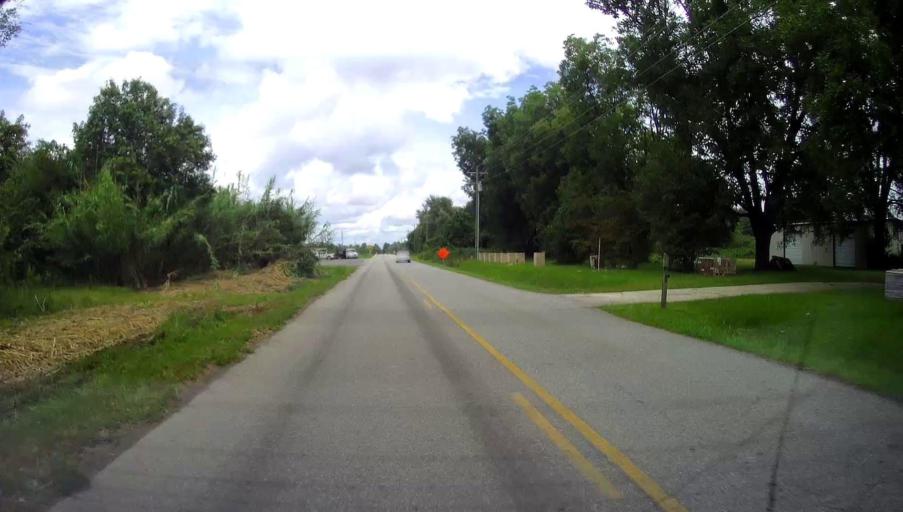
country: US
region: Georgia
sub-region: Peach County
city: Byron
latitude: 32.6056
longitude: -83.7481
